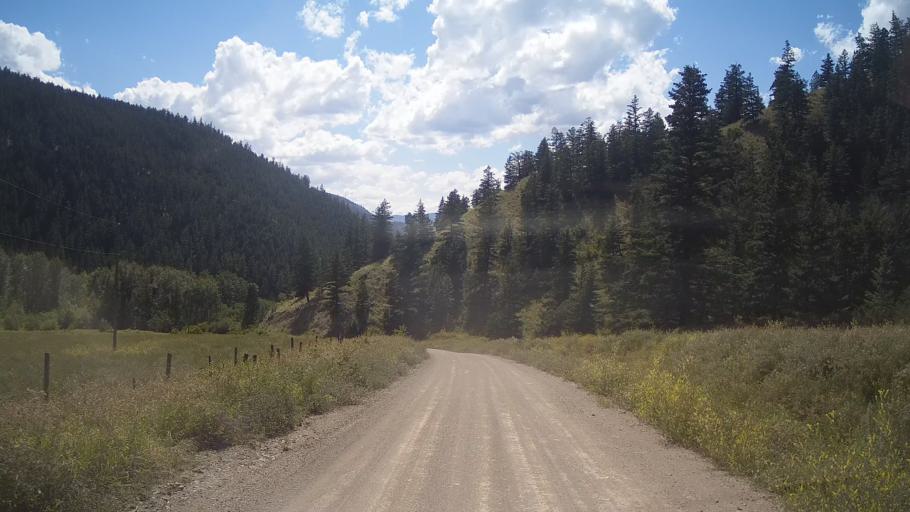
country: CA
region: British Columbia
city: Lillooet
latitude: 51.2493
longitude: -122.0258
